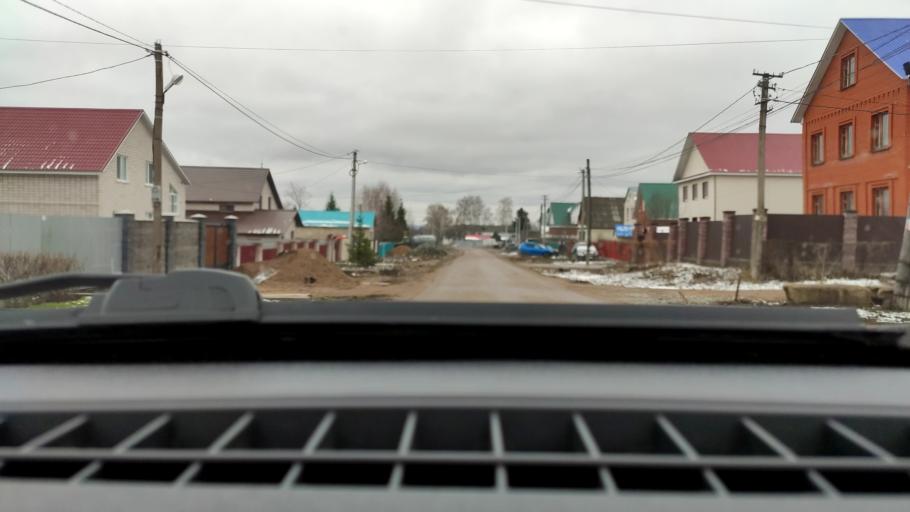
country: RU
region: Bashkortostan
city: Mikhaylovka
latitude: 54.8101
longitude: 55.8033
